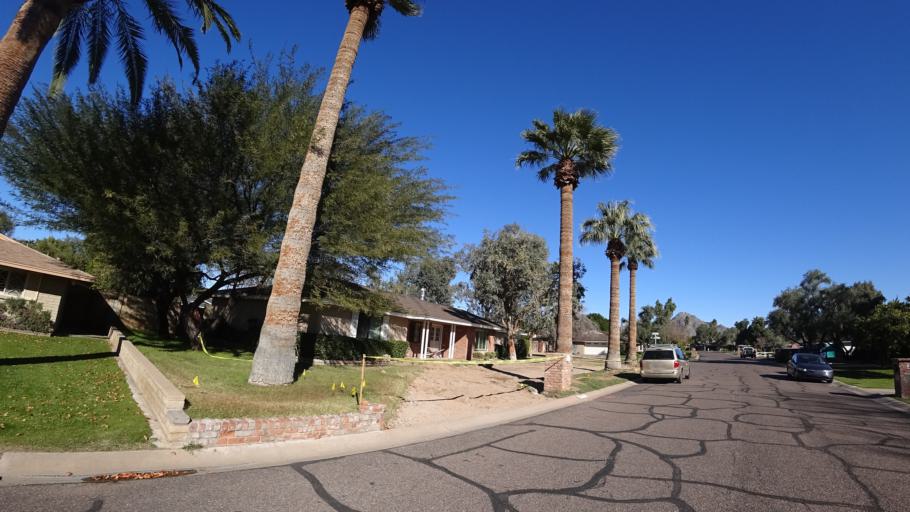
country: US
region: Arizona
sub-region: Maricopa County
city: Phoenix
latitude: 33.5442
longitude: -112.0686
